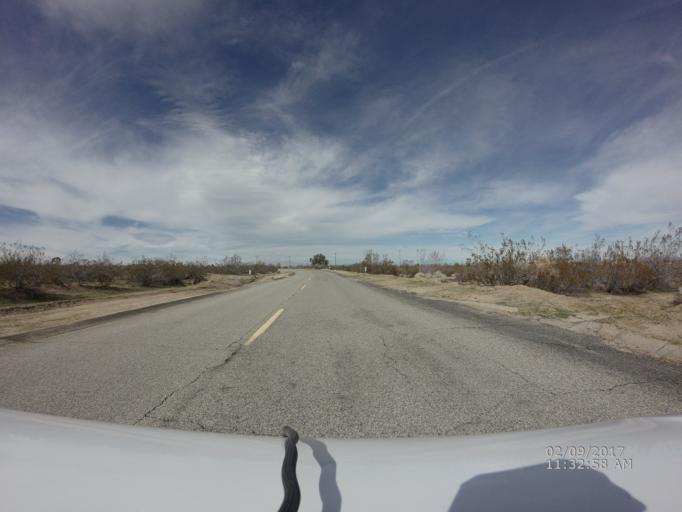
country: US
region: California
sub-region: Los Angeles County
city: Littlerock
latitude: 34.5200
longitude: -117.9268
